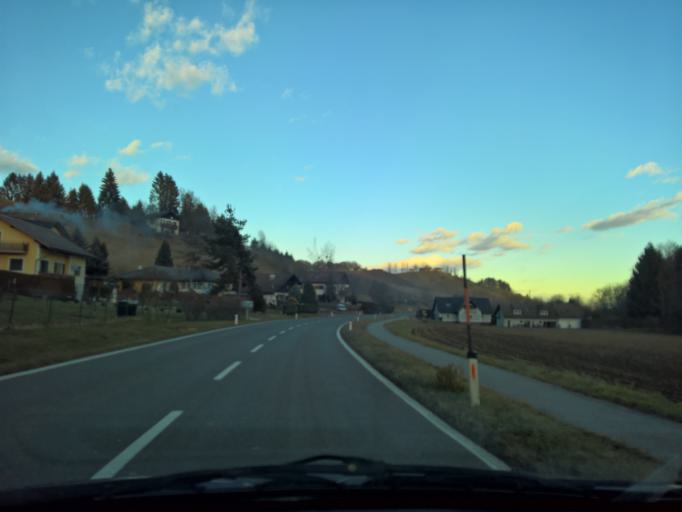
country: AT
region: Styria
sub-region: Politischer Bezirk Leibnitz
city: Gamlitz
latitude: 46.7153
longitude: 15.5106
